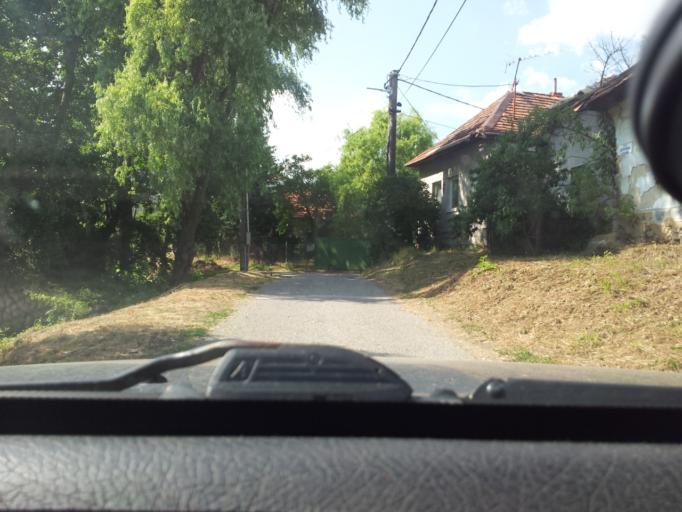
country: SK
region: Nitriansky
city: Tlmace
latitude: 48.3587
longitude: 18.5303
